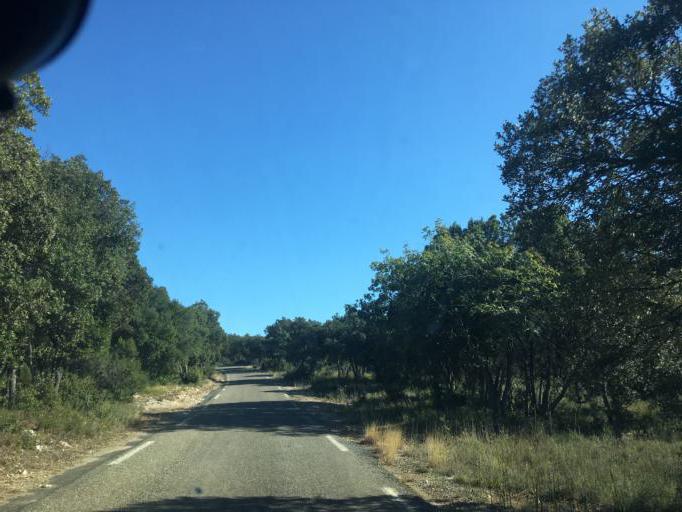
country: FR
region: Provence-Alpes-Cote d'Azur
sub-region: Departement du Var
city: Regusse
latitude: 43.7340
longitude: 6.1037
